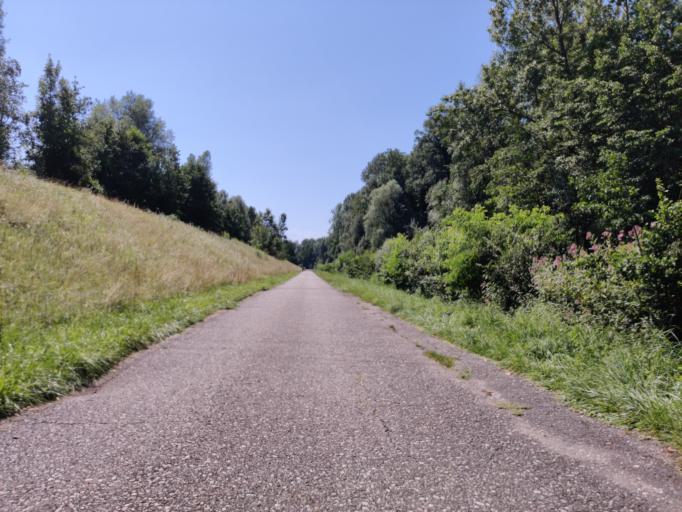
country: AT
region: Styria
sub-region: Politischer Bezirk Leibnitz
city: Gabersdorf
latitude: 46.7891
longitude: 15.5839
